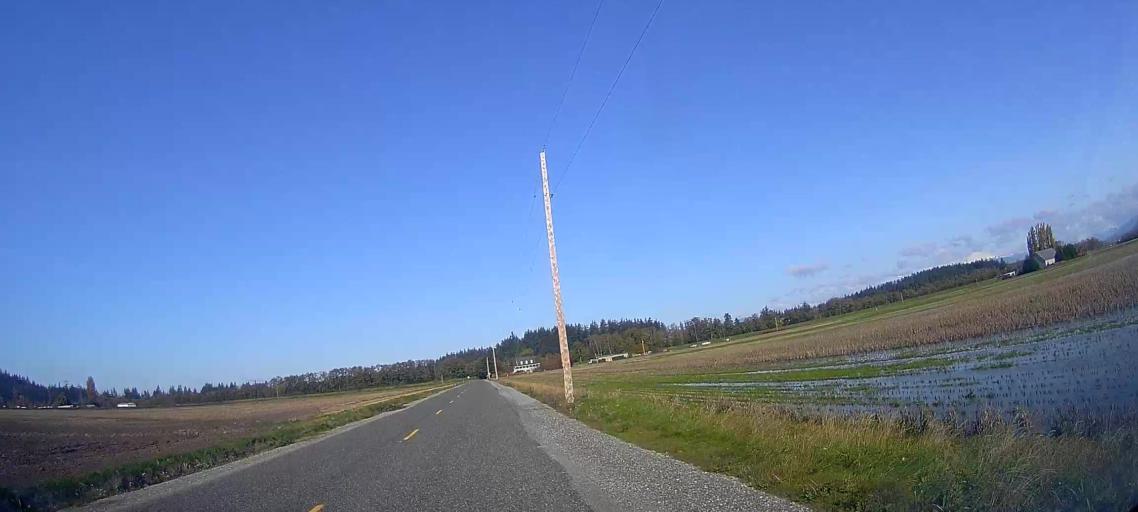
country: US
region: Washington
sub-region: Skagit County
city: Mount Vernon
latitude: 48.3518
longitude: -122.4387
